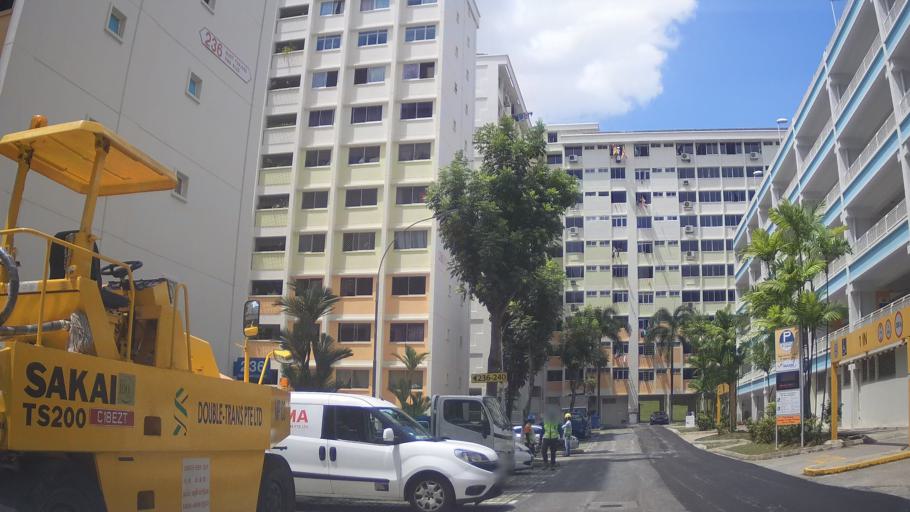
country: MY
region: Johor
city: Johor Bahru
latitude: 1.3788
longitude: 103.7718
